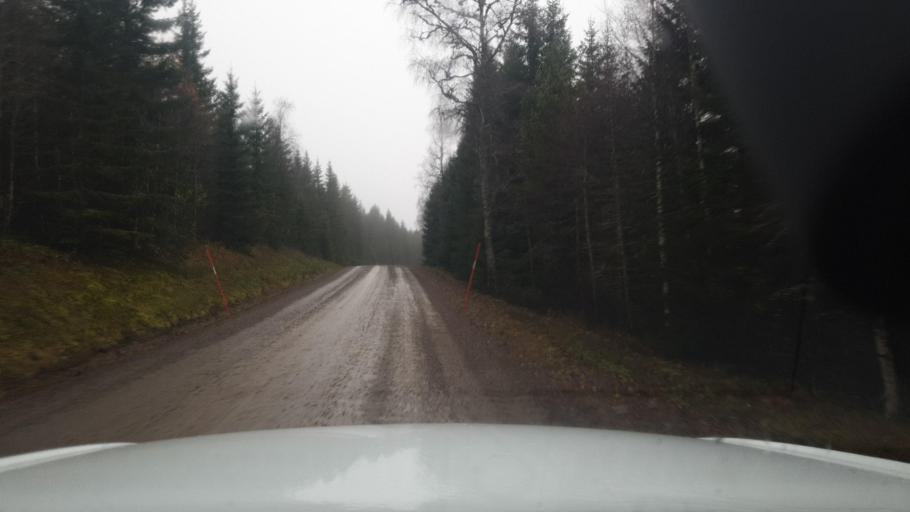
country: SE
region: Vaermland
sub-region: Sunne Kommun
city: Sunne
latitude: 59.8237
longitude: 12.8724
